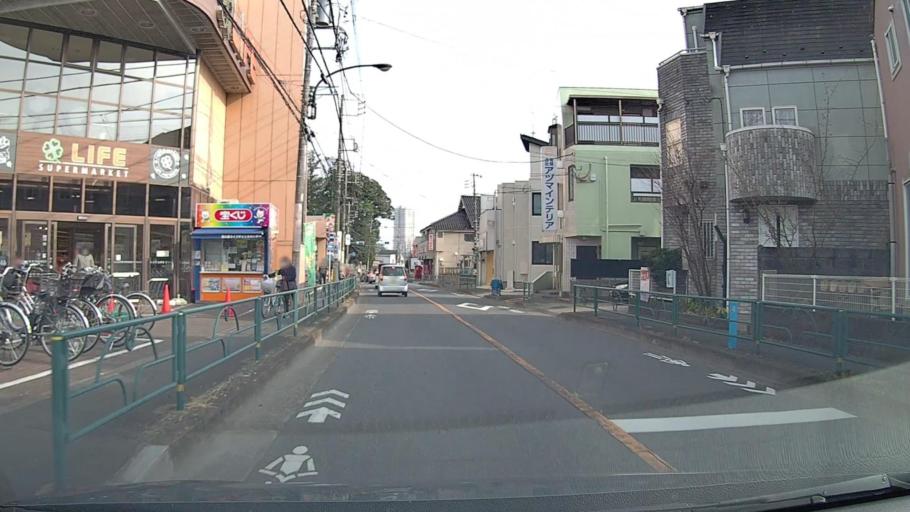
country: JP
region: Tokyo
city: Nishi-Tokyo-shi
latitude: 35.7566
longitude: 139.5789
